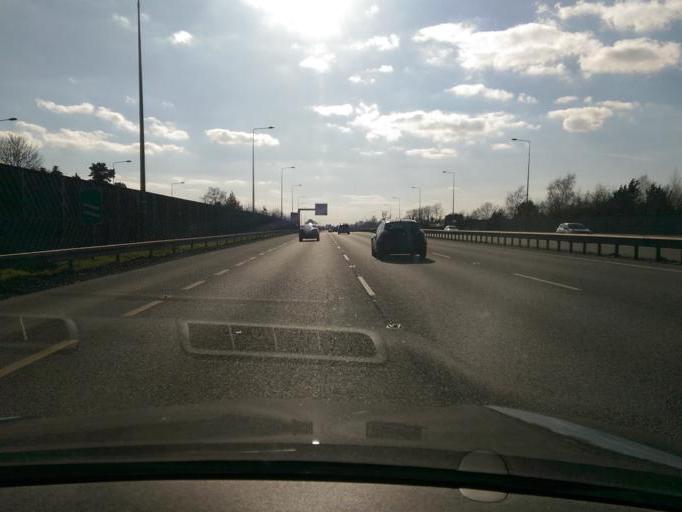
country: IE
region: Leinster
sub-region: Kildare
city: Kill
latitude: 53.2449
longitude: -6.6038
